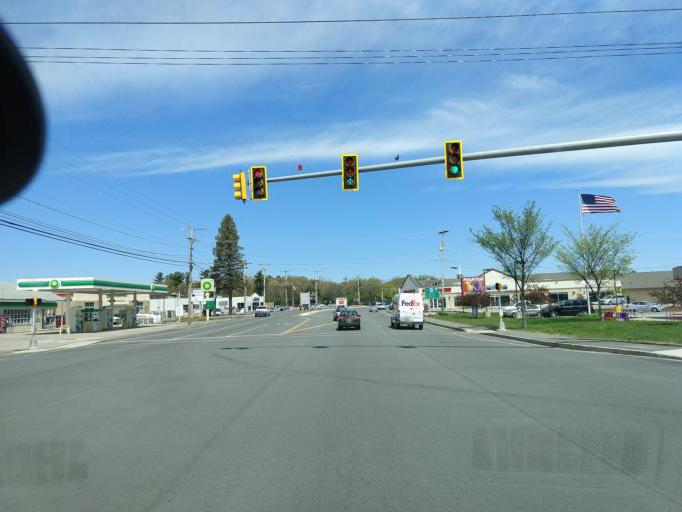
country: US
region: New Hampshire
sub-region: Rockingham County
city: Seabrook
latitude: 42.8915
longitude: -70.8723
